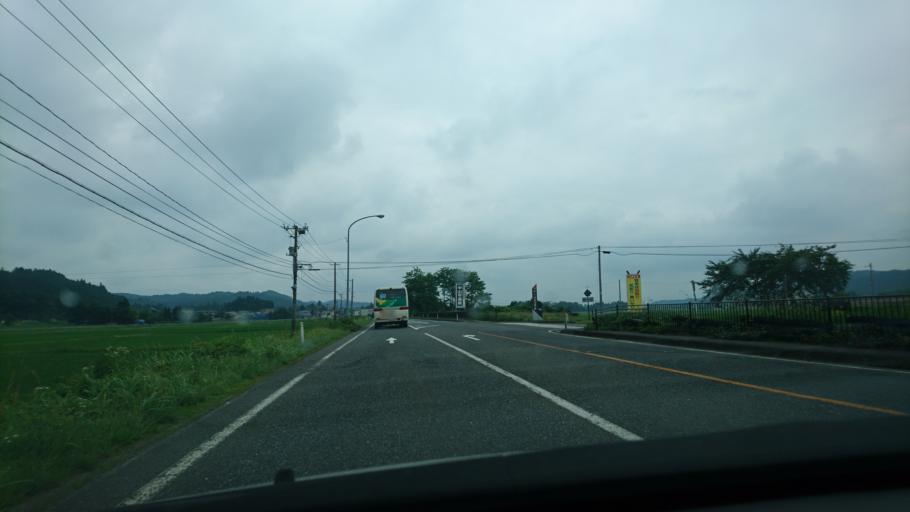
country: JP
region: Miyagi
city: Furukawa
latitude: 38.7156
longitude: 140.8243
